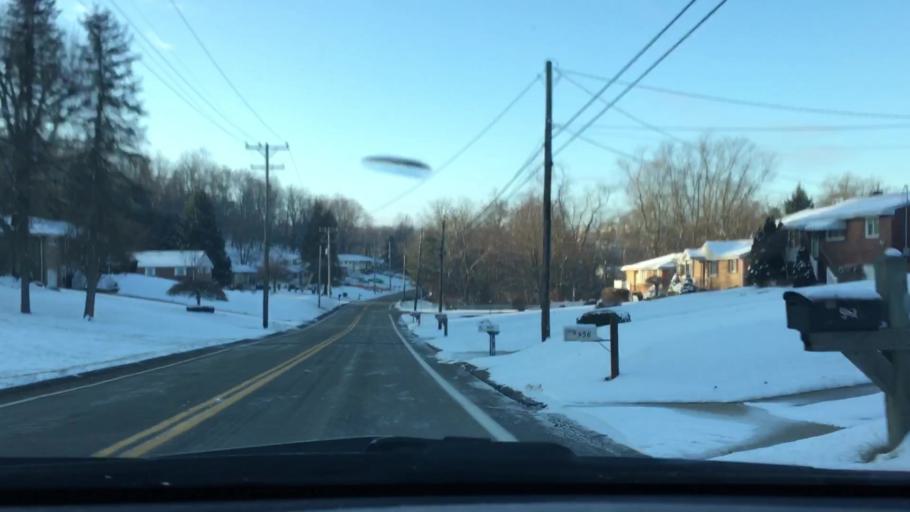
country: US
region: Pennsylvania
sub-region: Allegheny County
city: Elizabeth
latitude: 40.2675
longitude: -79.8497
